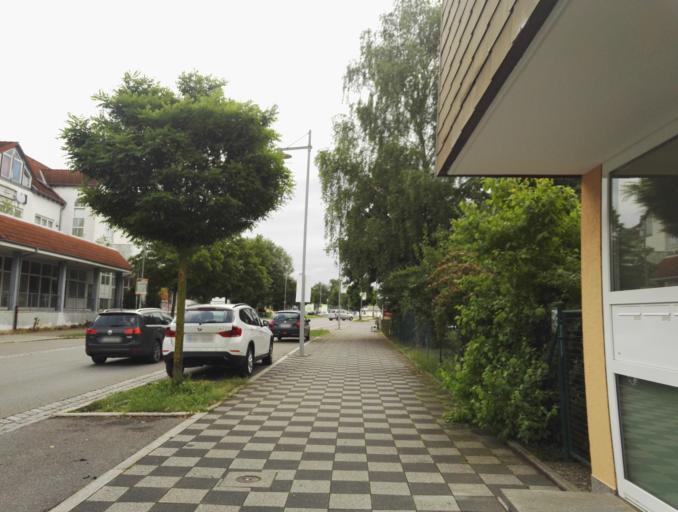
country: DE
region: Baden-Wuerttemberg
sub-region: Freiburg Region
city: Blumberg
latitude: 47.8396
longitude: 8.5370
